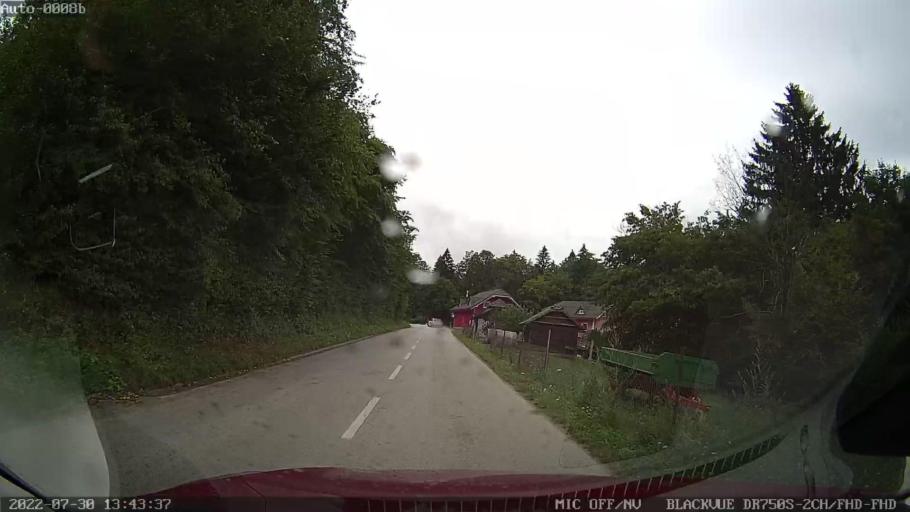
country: SI
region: Ivancna Gorica
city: Sentvid pri Sticni
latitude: 45.9136
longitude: 14.8954
